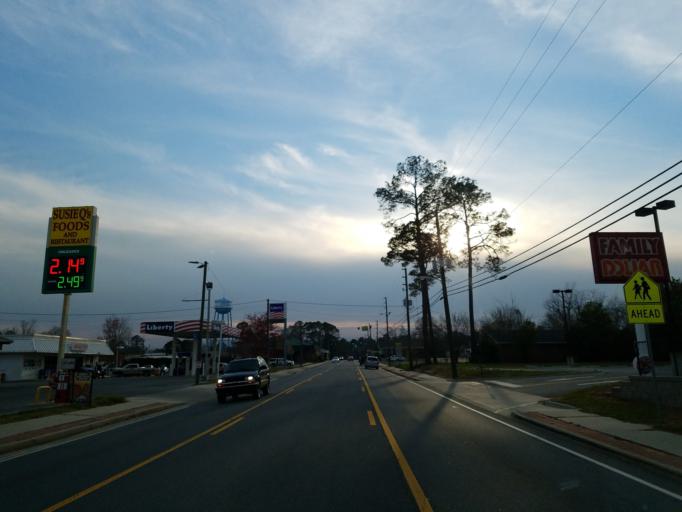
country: US
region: Georgia
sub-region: Tift County
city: Omega
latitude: 31.3409
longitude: -83.5940
